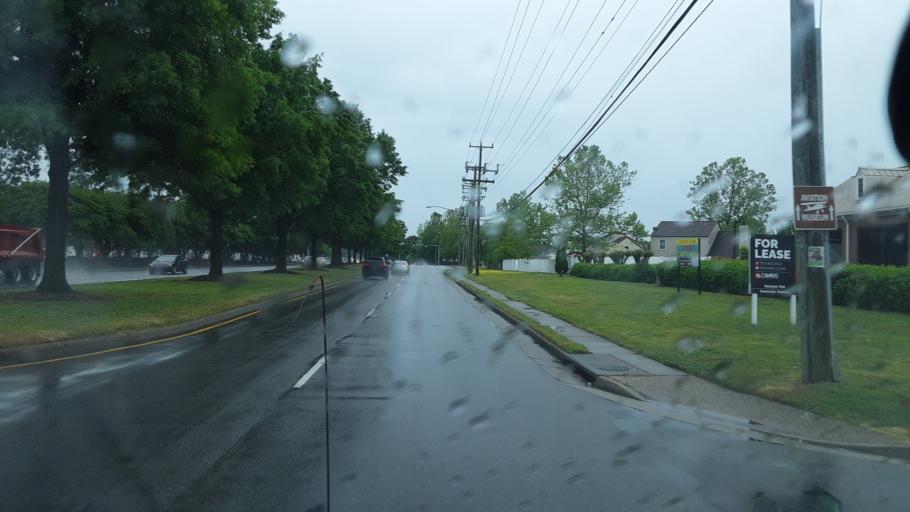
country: US
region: Virginia
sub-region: City of Virginia Beach
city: Virginia Beach
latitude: 36.7843
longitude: -76.0005
